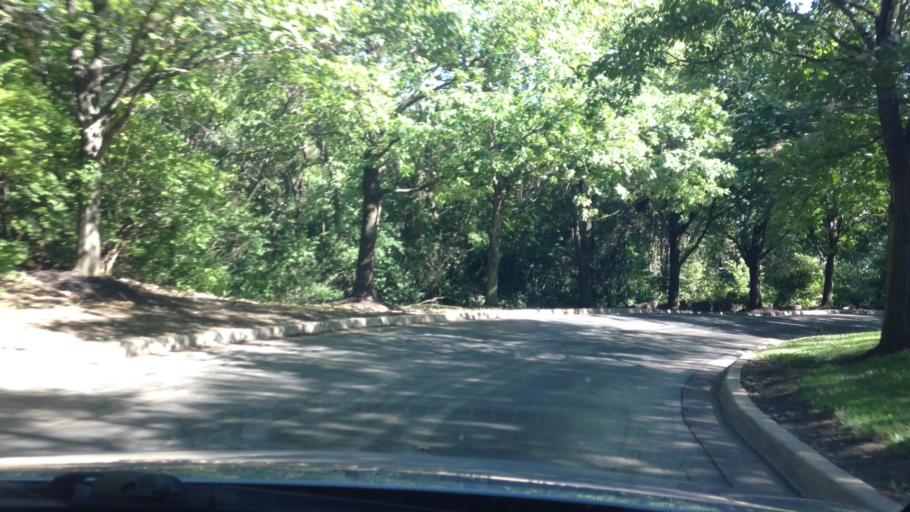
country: US
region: Kansas
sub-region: Johnson County
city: Roeland Park
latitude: 39.0464
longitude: -94.6416
